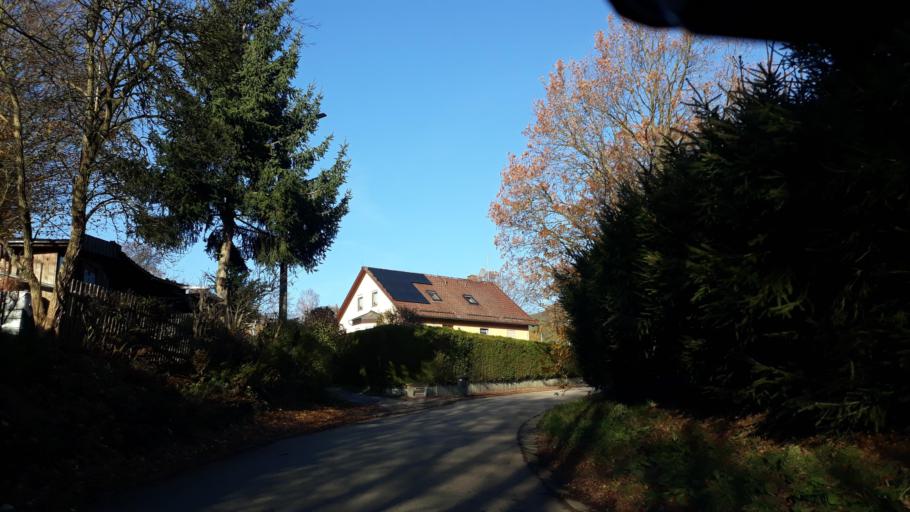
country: DE
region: Saxony
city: Kirchberg
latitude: 50.6470
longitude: 12.5141
